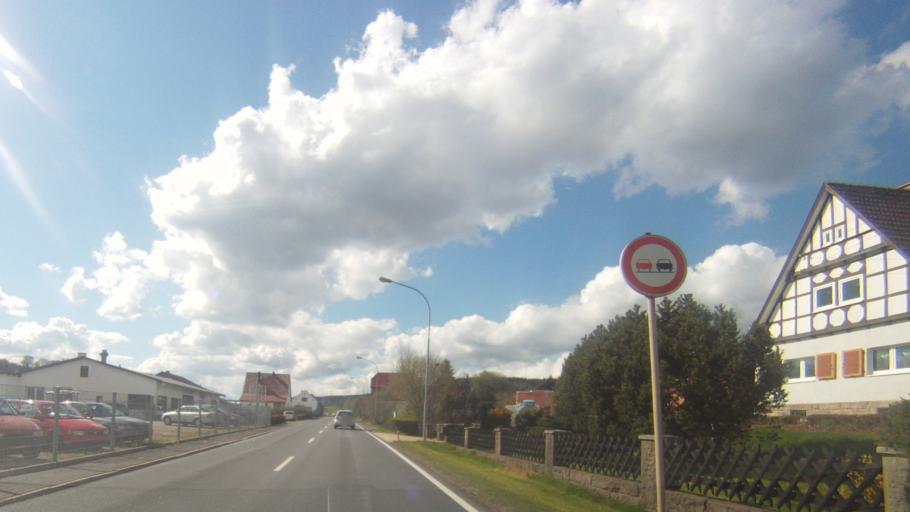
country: DE
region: Thuringia
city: Schalkau
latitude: 50.3866
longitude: 11.0575
